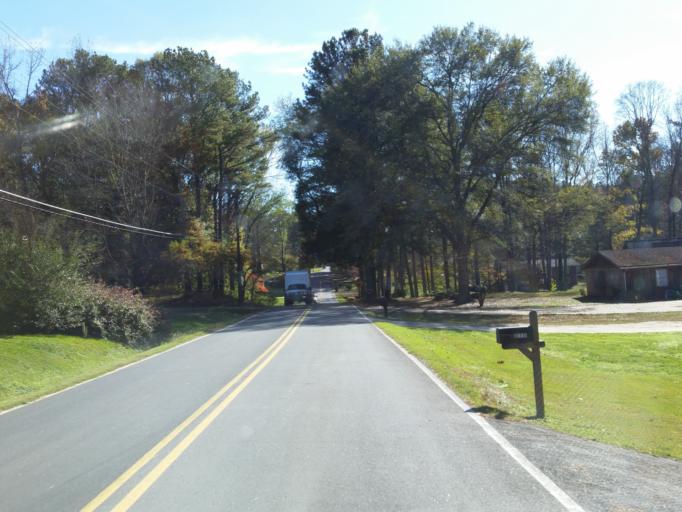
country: US
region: Georgia
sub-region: Cherokee County
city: Woodstock
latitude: 34.0291
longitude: -84.4858
